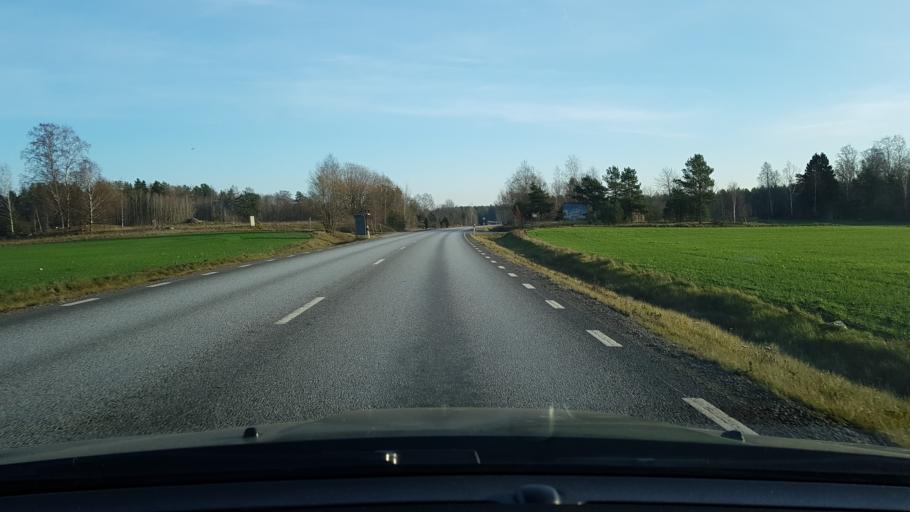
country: SE
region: Stockholm
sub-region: Vallentuna Kommun
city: Vallentuna
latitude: 59.7490
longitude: 18.0671
